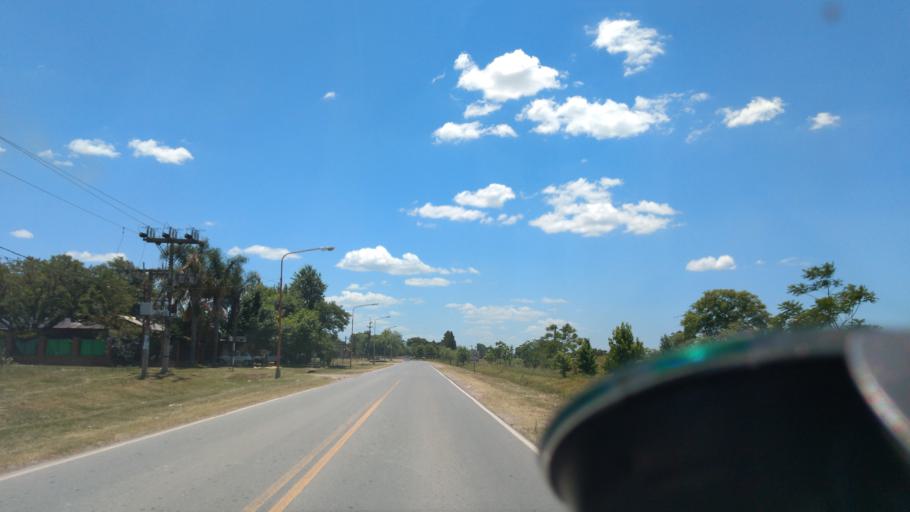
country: AR
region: Santa Fe
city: Laguna Paiva
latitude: -31.3168
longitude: -60.6585
